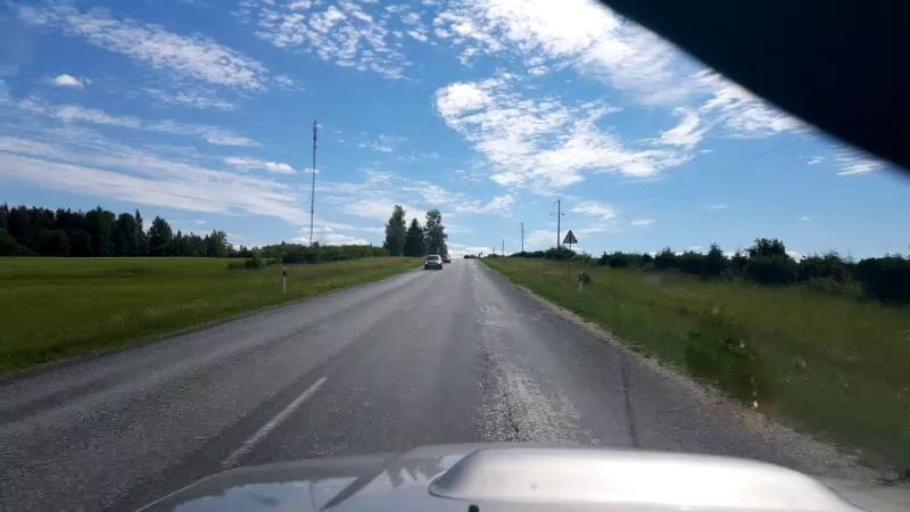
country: EE
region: Laeaene-Virumaa
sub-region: Rakke vald
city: Rakke
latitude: 58.8528
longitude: 26.2919
